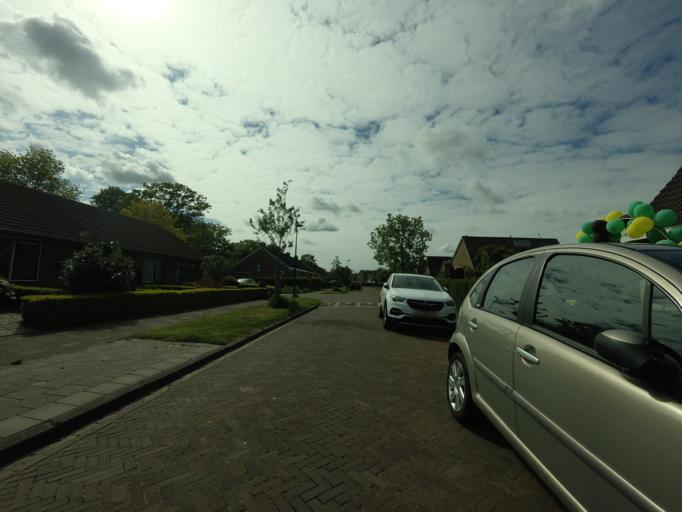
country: NL
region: Friesland
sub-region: Sudwest Fryslan
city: Heeg
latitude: 52.9931
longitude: 5.5506
